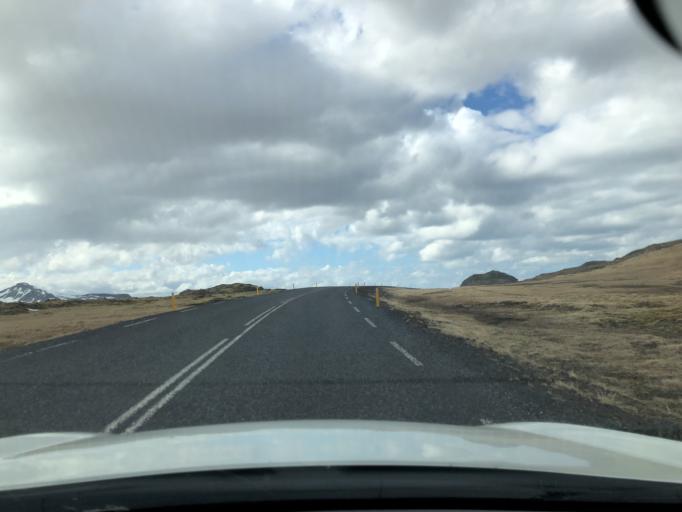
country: IS
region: West
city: Olafsvik
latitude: 64.8643
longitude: -23.5406
